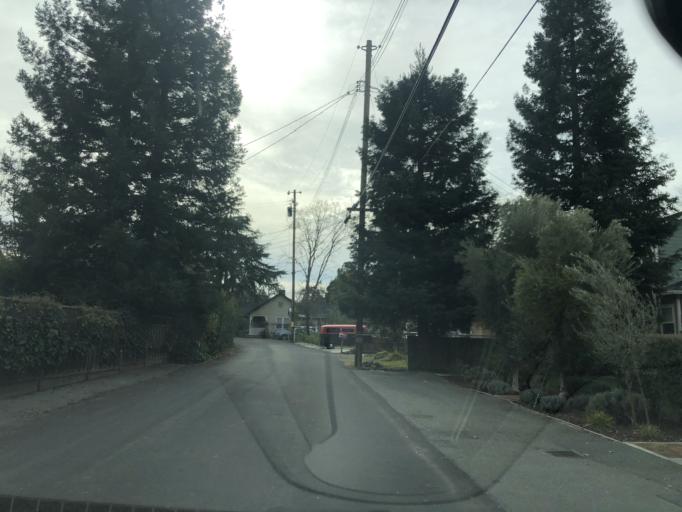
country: US
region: California
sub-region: Contra Costa County
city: Saranap
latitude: 37.8941
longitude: -122.0702
